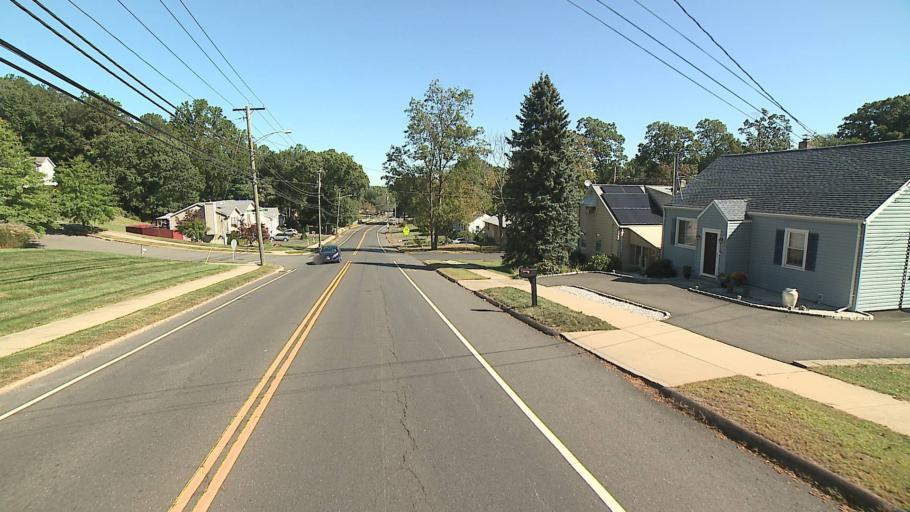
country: US
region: Connecticut
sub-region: New Haven County
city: West Haven
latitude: 41.2568
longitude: -72.9697
